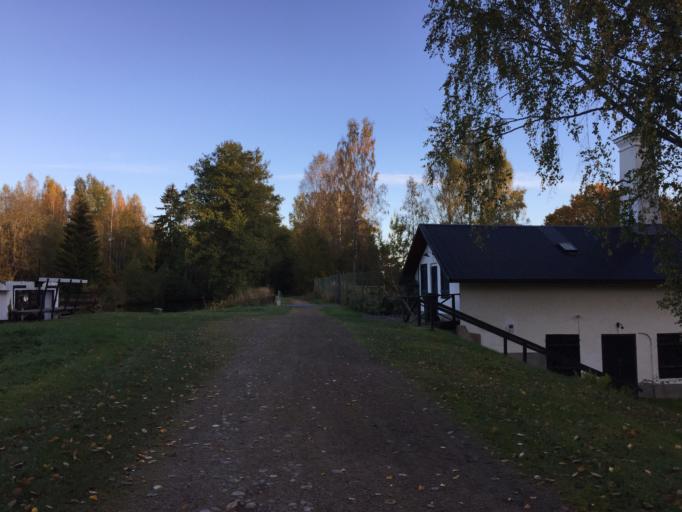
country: SE
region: Vaestmanland
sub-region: Hallstahammars Kommun
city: Hallstahammar
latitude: 59.6277
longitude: 16.2039
